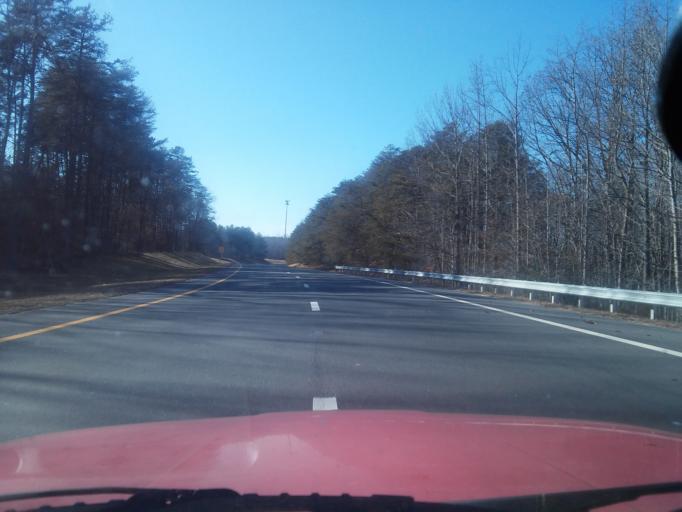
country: US
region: Virginia
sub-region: Fluvanna County
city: Palmyra
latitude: 37.9788
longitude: -78.2144
